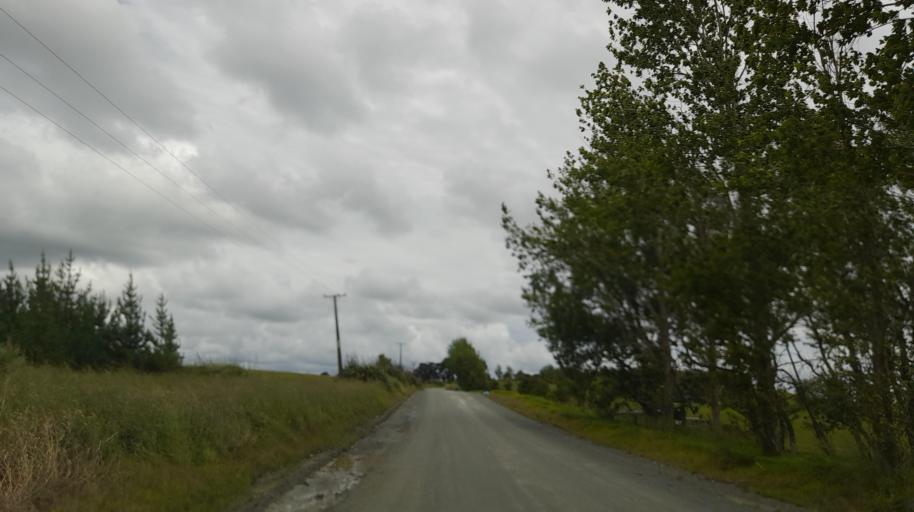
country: NZ
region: Auckland
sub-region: Auckland
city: Wellsford
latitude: -36.2368
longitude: 174.4382
